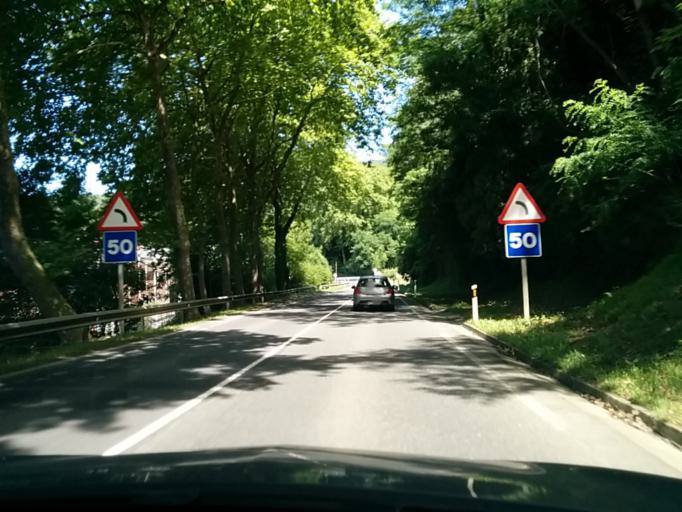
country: ES
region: Basque Country
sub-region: Provincia de Guipuzcoa
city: Usurbil
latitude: 43.2753
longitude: -2.0560
